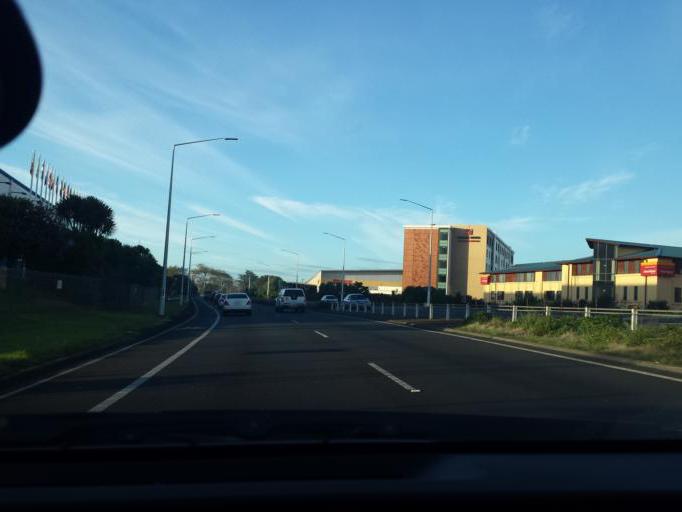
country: NZ
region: Auckland
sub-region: Auckland
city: Mangere
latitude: -36.9832
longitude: 174.7845
